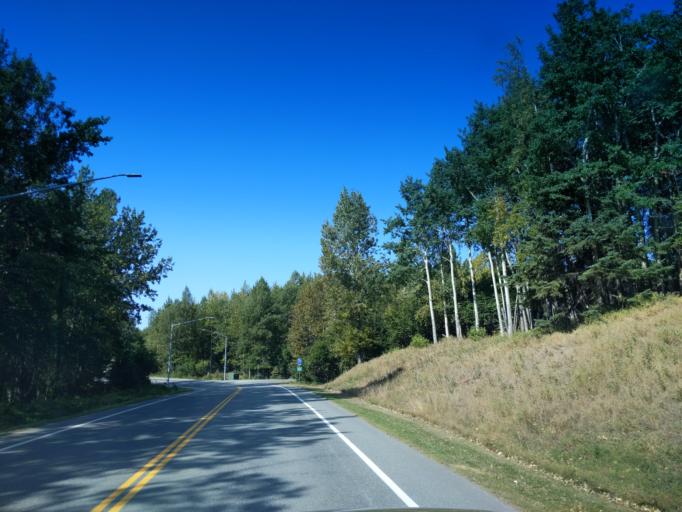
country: US
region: Alaska
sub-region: Anchorage Municipality
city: Anchorage
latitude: 61.1551
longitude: -150.0360
